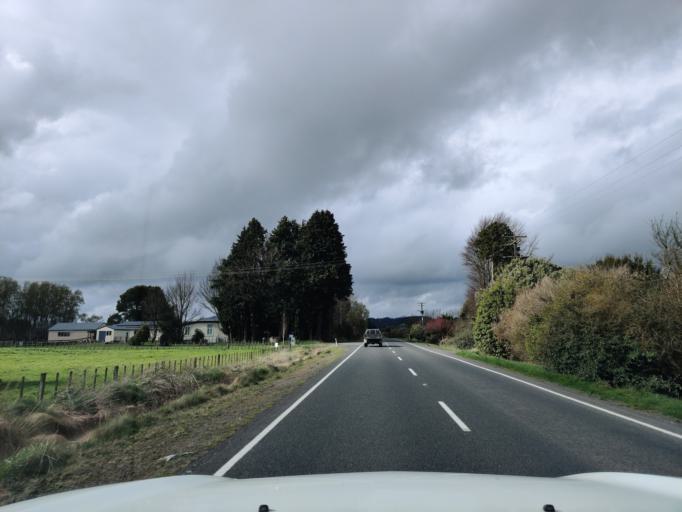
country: NZ
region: Manawatu-Wanganui
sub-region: Ruapehu District
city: Waiouru
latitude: -39.3747
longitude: 175.3098
